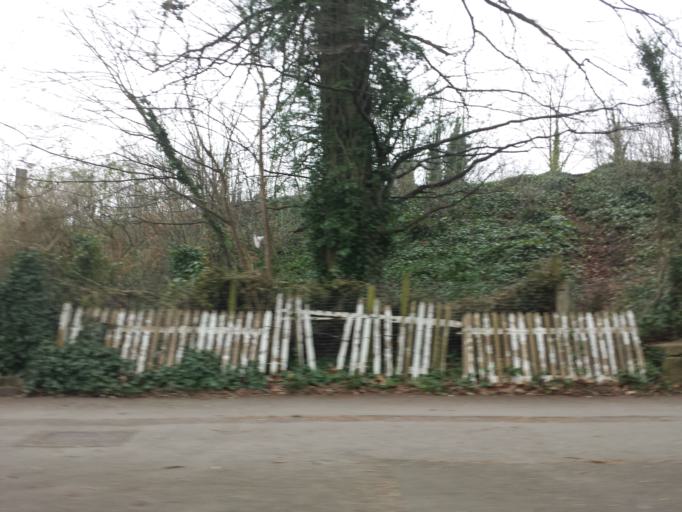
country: GB
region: England
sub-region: Bath and North East Somerset
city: Bath
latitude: 51.3803
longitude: -2.3513
